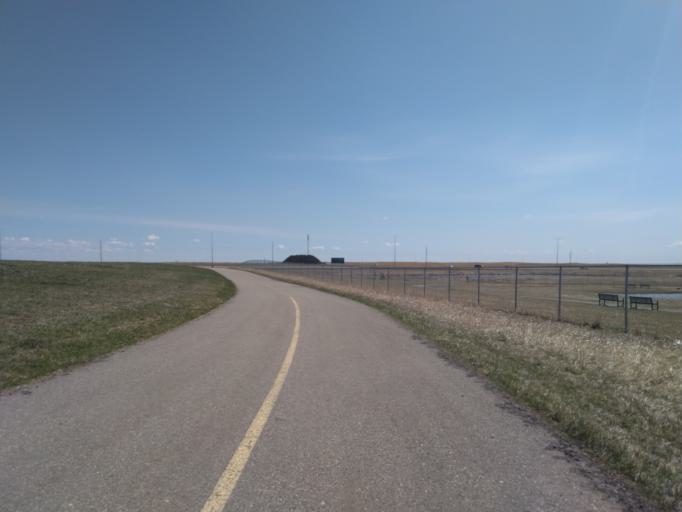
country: CA
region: Alberta
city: Chestermere
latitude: 51.1108
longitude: -113.9248
